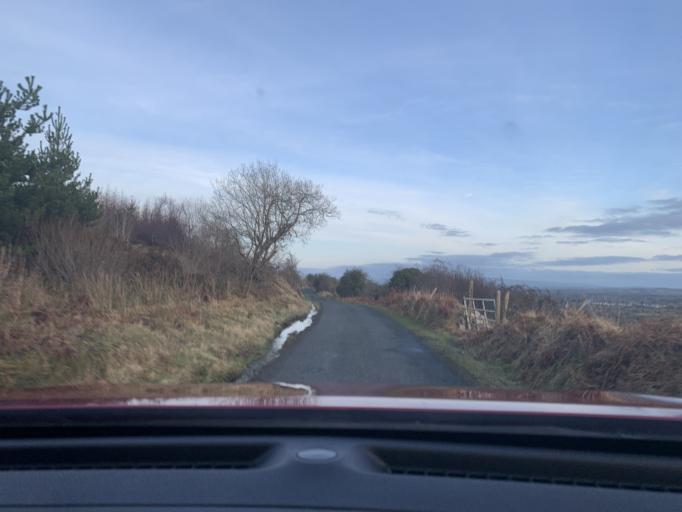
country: IE
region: Connaught
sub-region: Sligo
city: Strandhill
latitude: 54.1767
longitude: -8.6429
